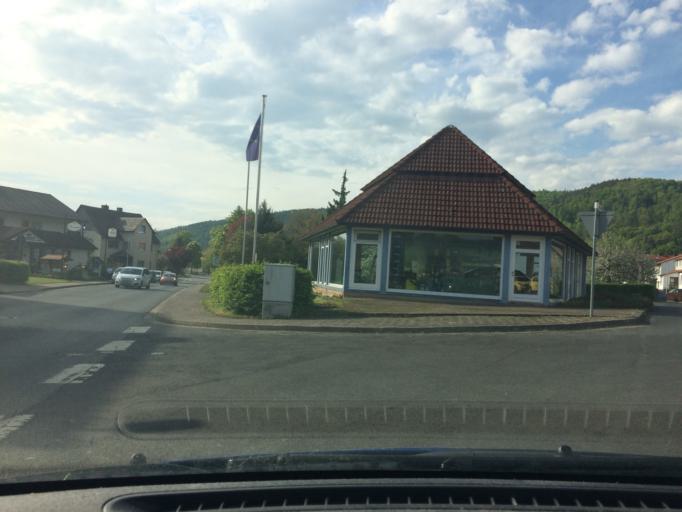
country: DE
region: Lower Saxony
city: Bodenfelde
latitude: 51.5920
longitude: 9.5934
